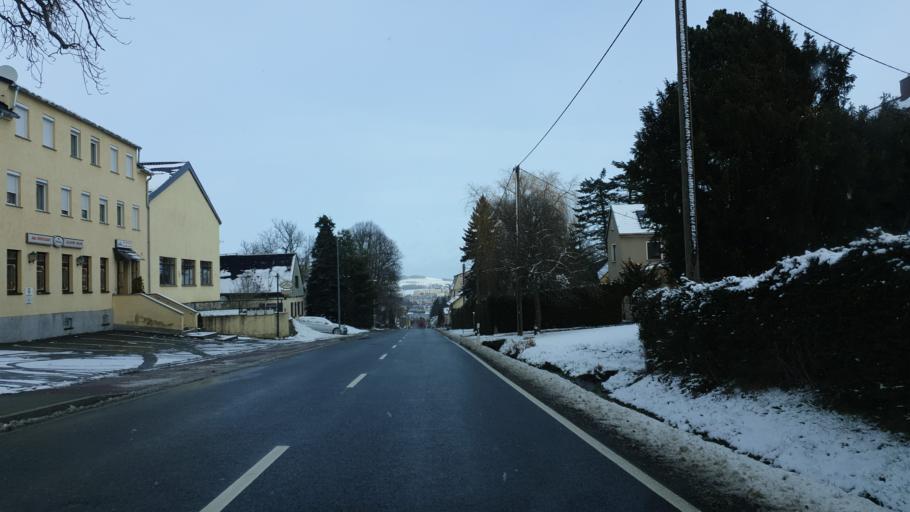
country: DE
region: Saxony
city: Oelsnitz
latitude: 50.3983
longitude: 12.1531
